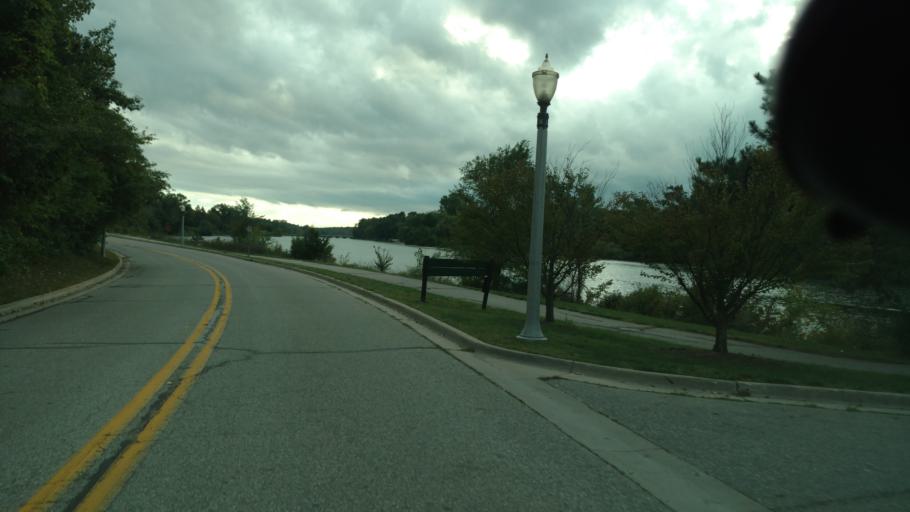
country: US
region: Michigan
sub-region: Ingham County
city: Edgemont Park
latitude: 42.7179
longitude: -84.5926
